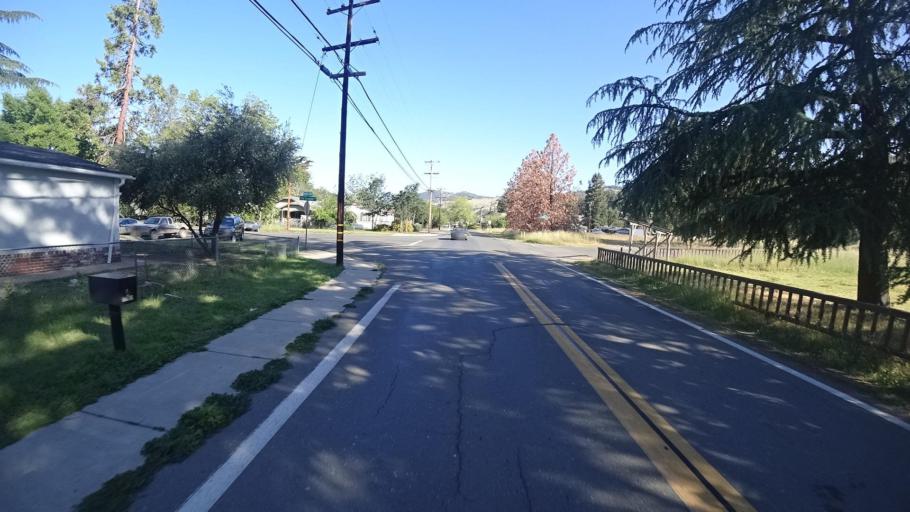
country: US
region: California
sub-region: Lake County
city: Lucerne
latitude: 39.0887
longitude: -122.7901
